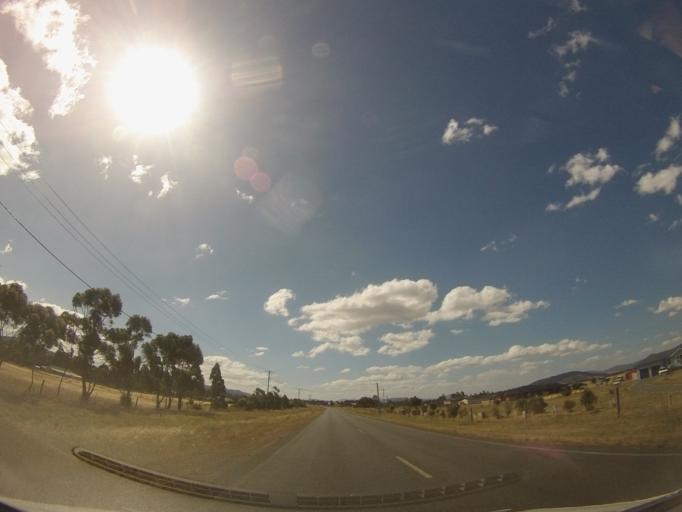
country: AU
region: Tasmania
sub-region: Clarence
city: Seven Mile Beach
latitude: -42.8512
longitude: 147.4850
